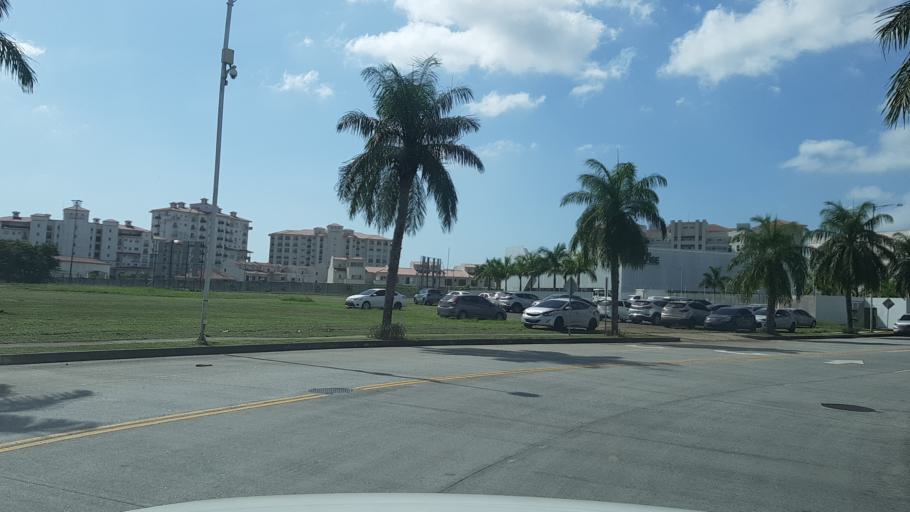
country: PA
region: Panama
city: San Miguelito
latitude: 9.0304
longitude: -79.4575
